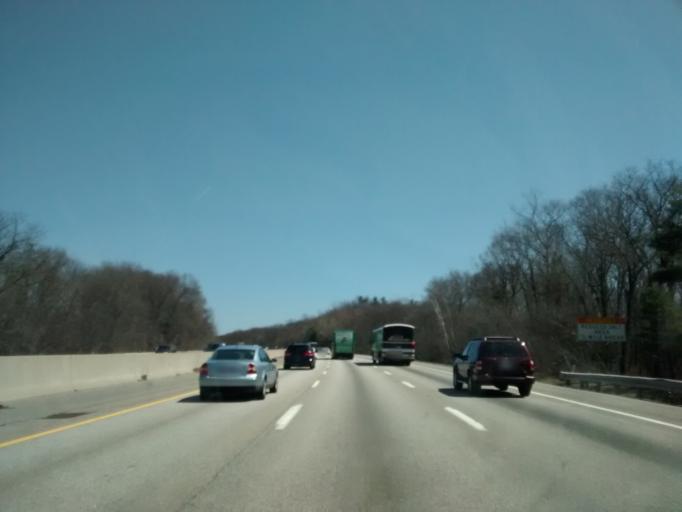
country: US
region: Massachusetts
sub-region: Worcester County
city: Westborough
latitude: 42.2265
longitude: -71.6340
